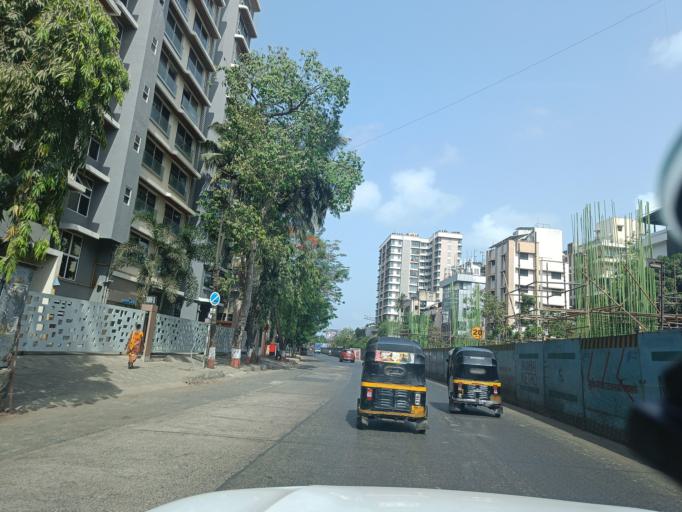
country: IN
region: Maharashtra
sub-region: Mumbai Suburban
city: Mumbai
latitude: 19.1159
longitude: 72.8338
